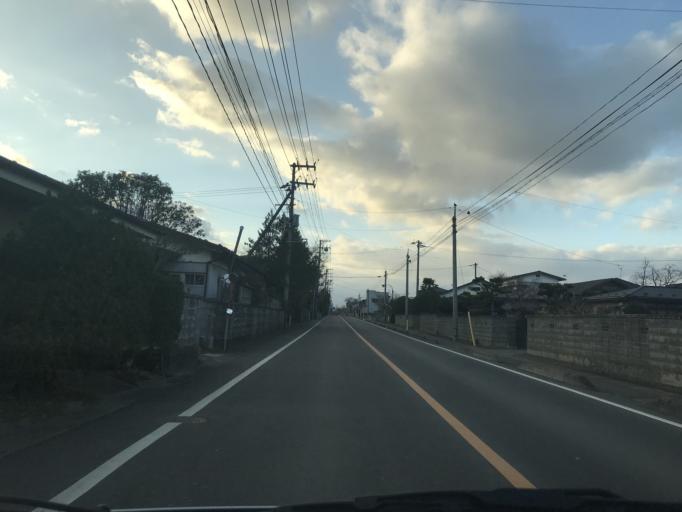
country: JP
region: Miyagi
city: Furukawa
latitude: 38.6585
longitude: 141.0176
